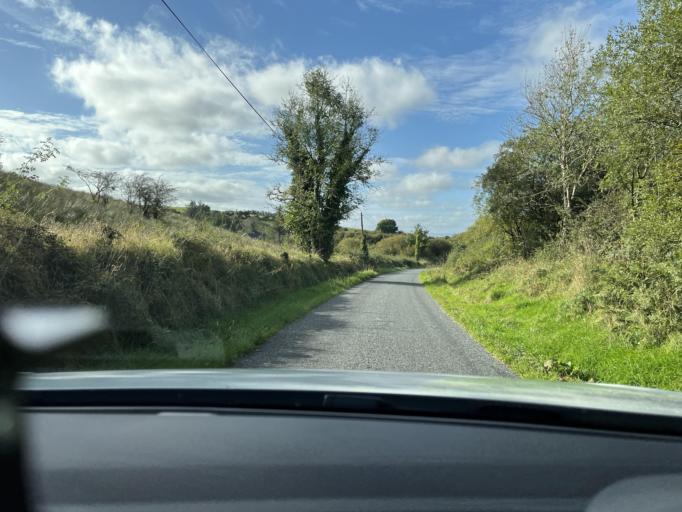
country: IE
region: Connaught
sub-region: Sligo
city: Ballymote
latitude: 54.0772
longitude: -8.4473
